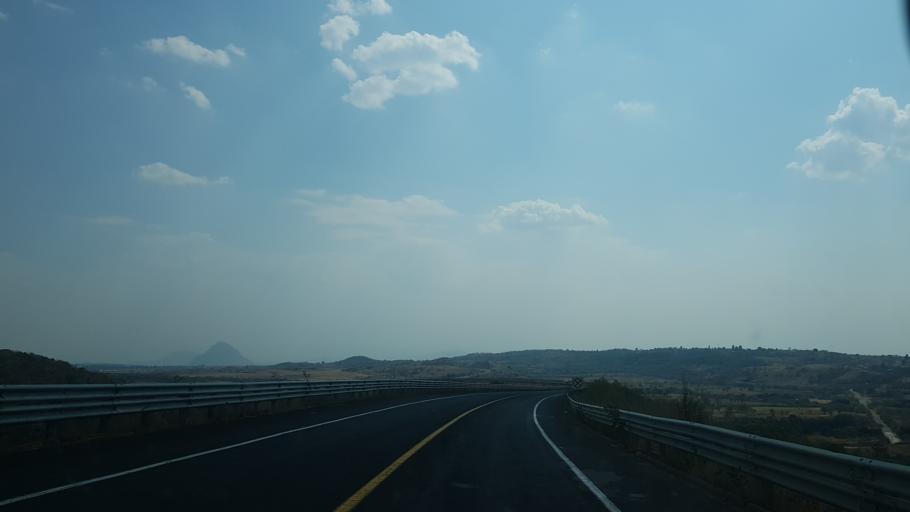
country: MX
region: Puebla
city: San Juan Amecac
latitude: 18.8206
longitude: -98.6909
